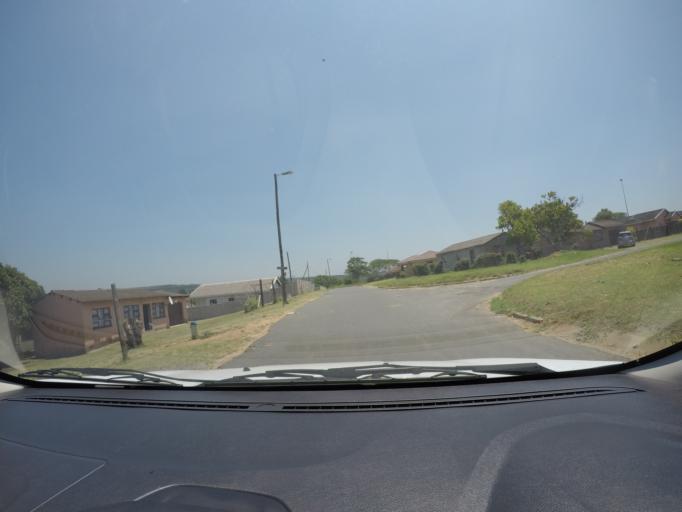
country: ZA
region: KwaZulu-Natal
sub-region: uThungulu District Municipality
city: eSikhawini
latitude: -28.8755
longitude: 31.9071
